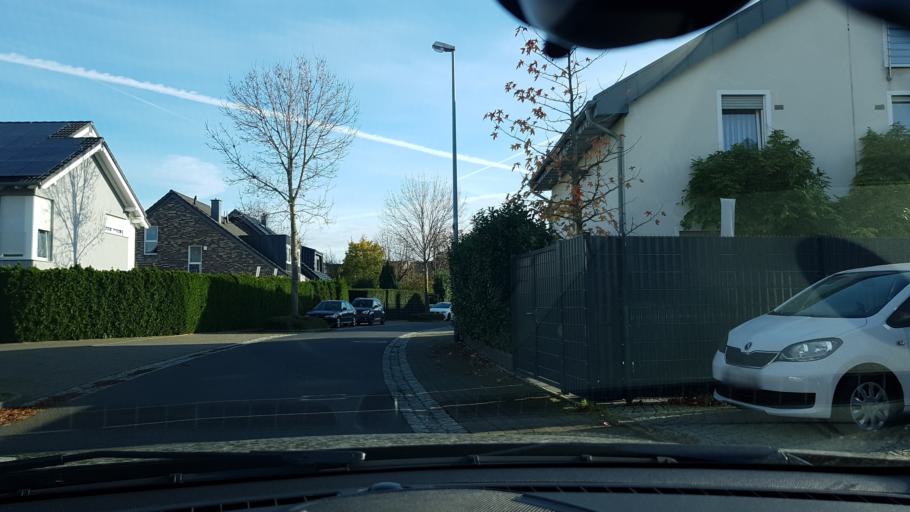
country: DE
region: North Rhine-Westphalia
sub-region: Regierungsbezirk Dusseldorf
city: Grevenbroich
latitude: 51.1151
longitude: 6.5619
